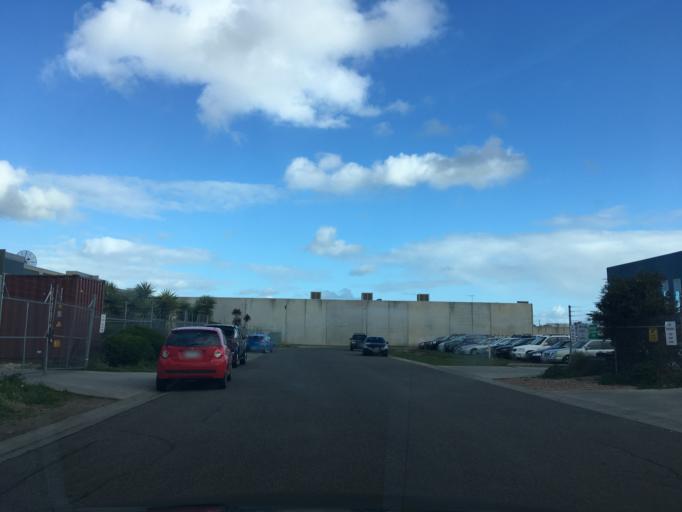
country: AU
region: Victoria
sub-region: Wyndham
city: Hoppers Crossing
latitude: -37.8719
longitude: 144.7170
